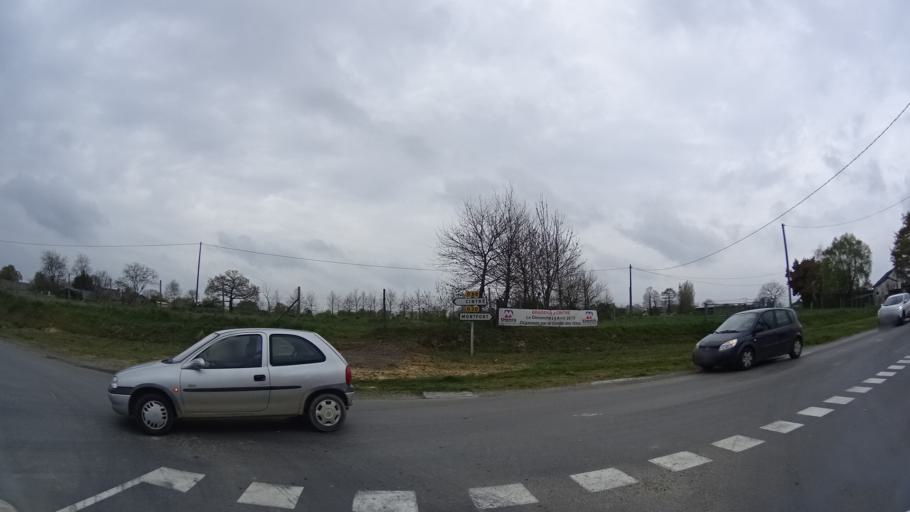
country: FR
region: Brittany
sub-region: Departement d'Ille-et-Vilaine
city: La Chapelle-Thouarault
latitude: 48.1213
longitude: -1.8723
